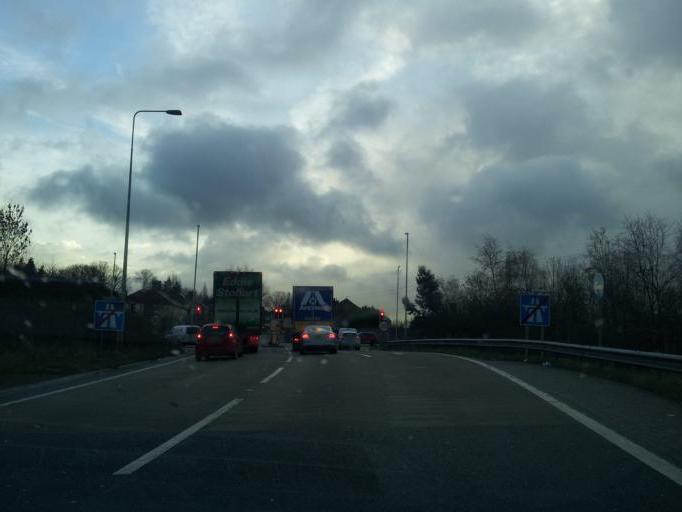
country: GB
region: England
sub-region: Borough of Rochdale
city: Middleton
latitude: 53.5349
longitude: -2.2075
